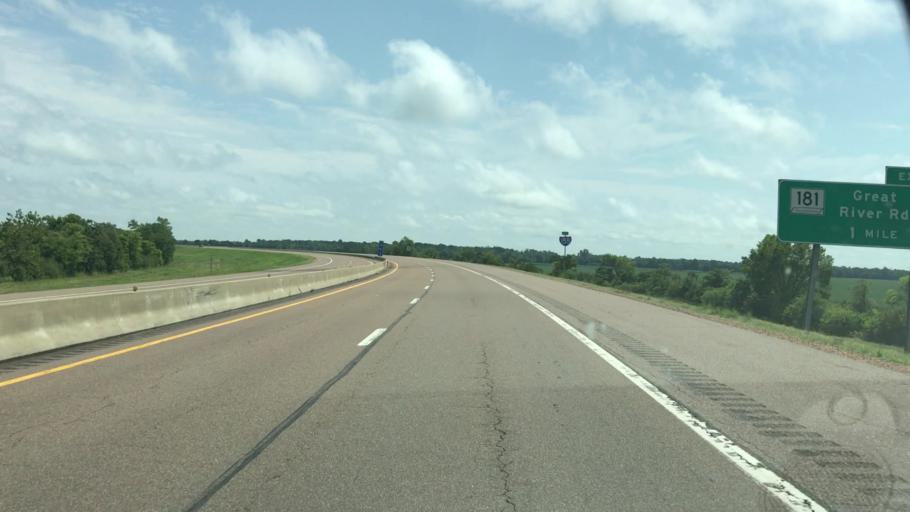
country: US
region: Missouri
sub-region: Pemiscot County
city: Caruthersville
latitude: 36.1007
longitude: -89.6049
